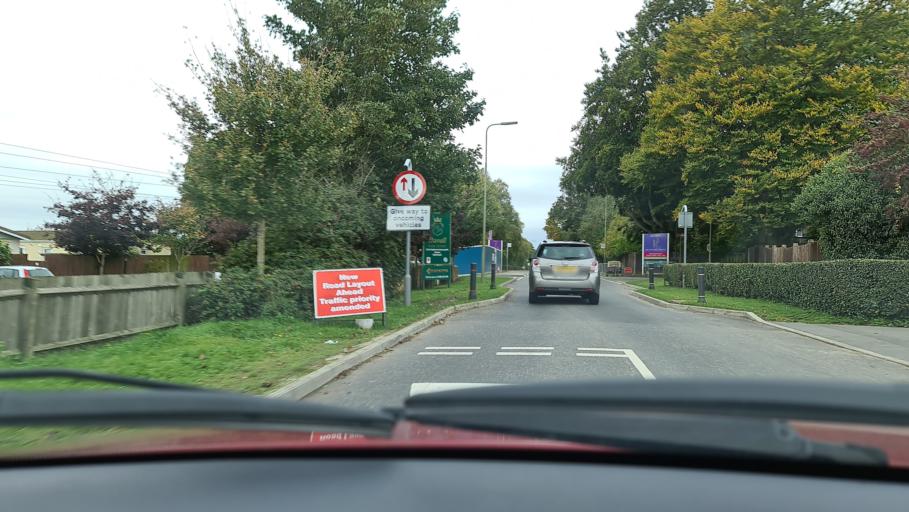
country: GB
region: England
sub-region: Oxfordshire
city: Somerton
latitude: 51.9276
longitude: -1.2472
